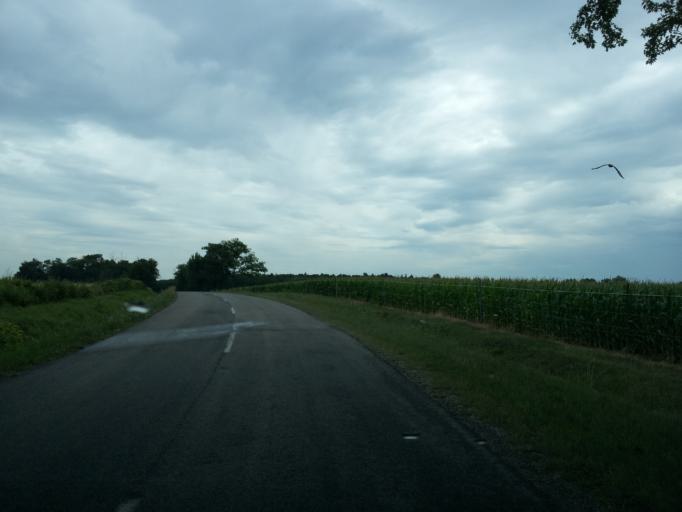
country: HU
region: Vas
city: Kormend
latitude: 46.9618
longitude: 16.6976
